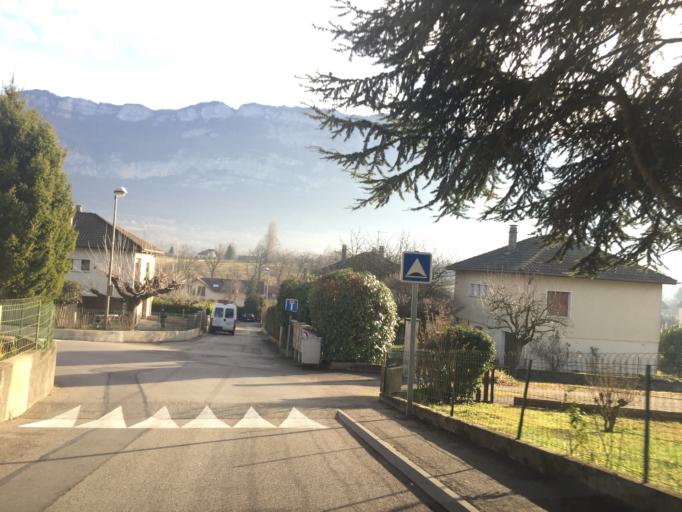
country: FR
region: Rhone-Alpes
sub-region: Departement de la Savoie
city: Viviers-du-Lac
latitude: 45.6526
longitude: 5.9060
